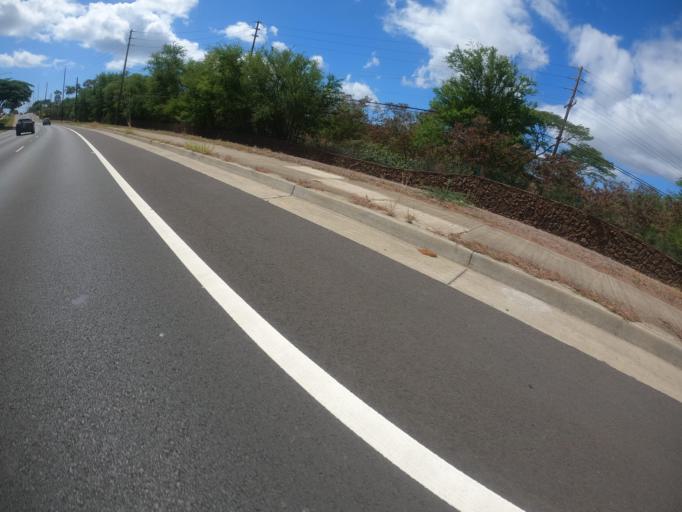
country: US
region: Hawaii
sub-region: Honolulu County
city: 'Ewa Gentry
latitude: 21.3579
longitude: -158.0297
